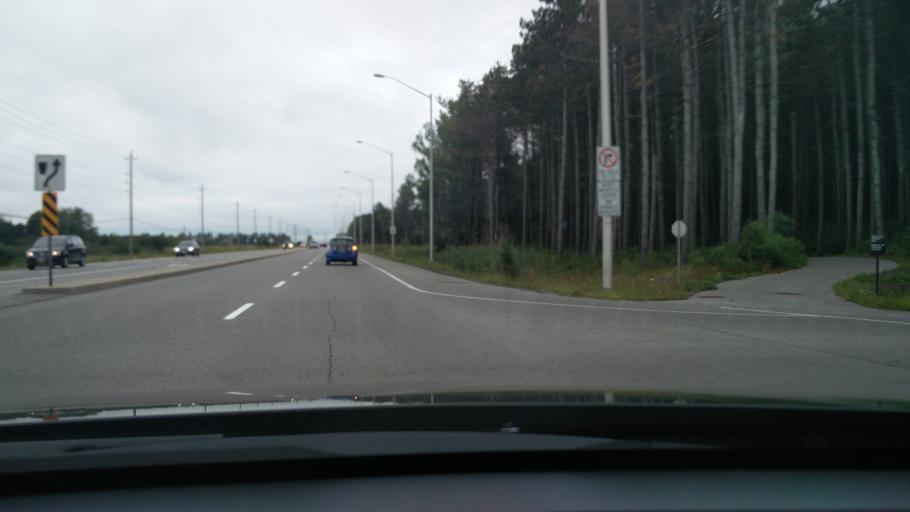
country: CA
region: Ontario
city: Bells Corners
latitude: 45.3105
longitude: -75.7379
